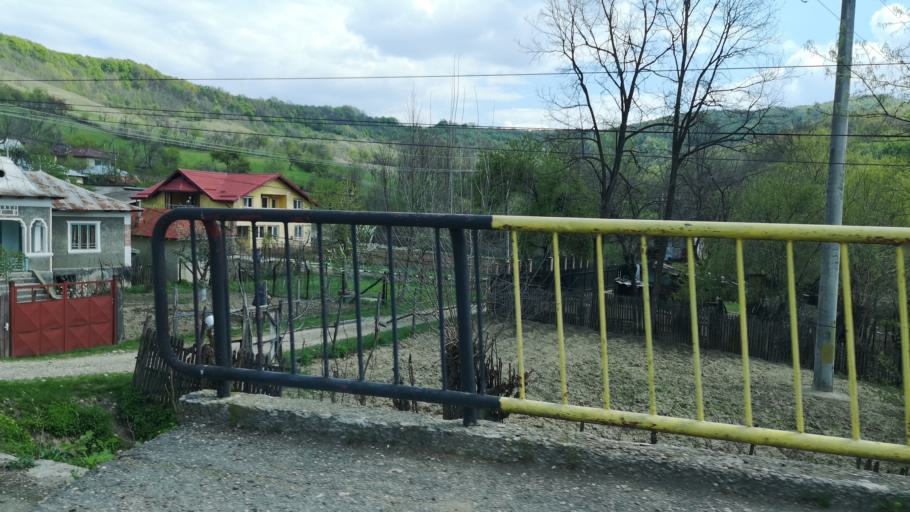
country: RO
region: Prahova
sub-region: Comuna Soimari
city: Soimari
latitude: 45.1701
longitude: 26.2127
